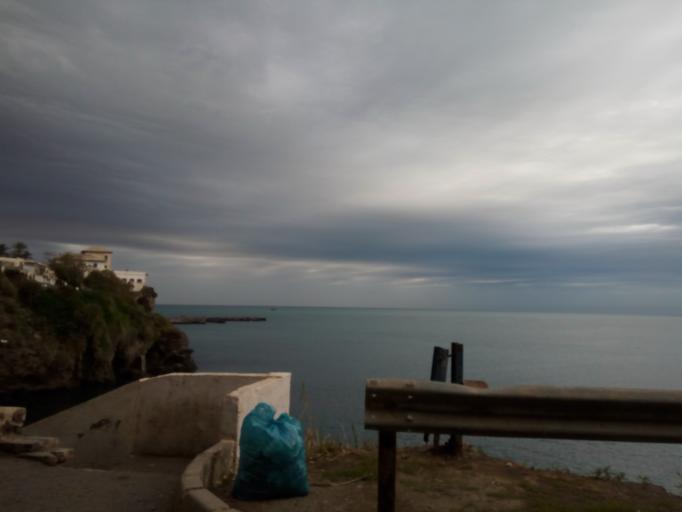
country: DZ
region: Alger
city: Algiers
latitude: 36.8137
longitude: 3.0196
